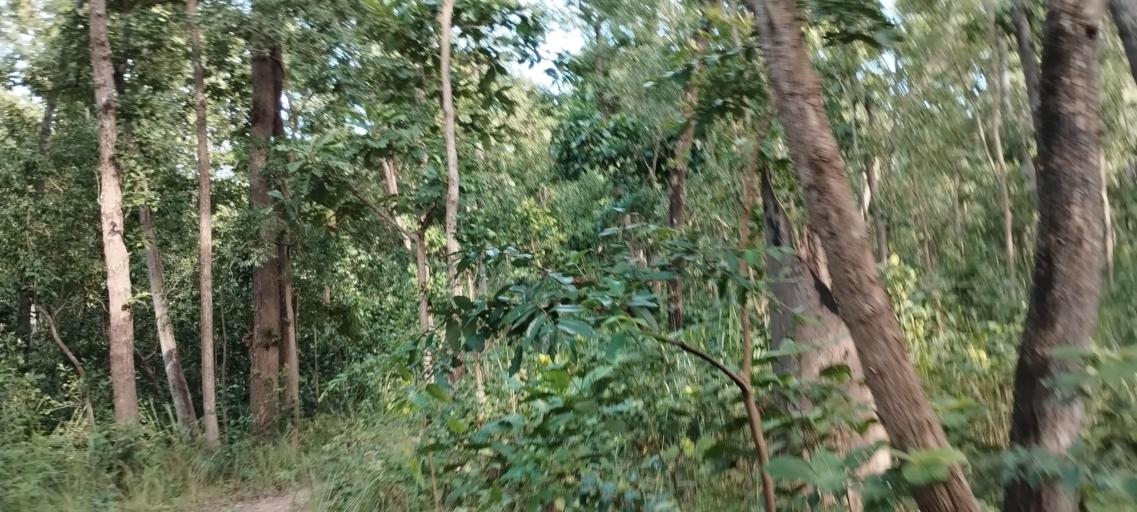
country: NP
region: Far Western
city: Tikapur
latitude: 28.5502
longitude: 81.2864
